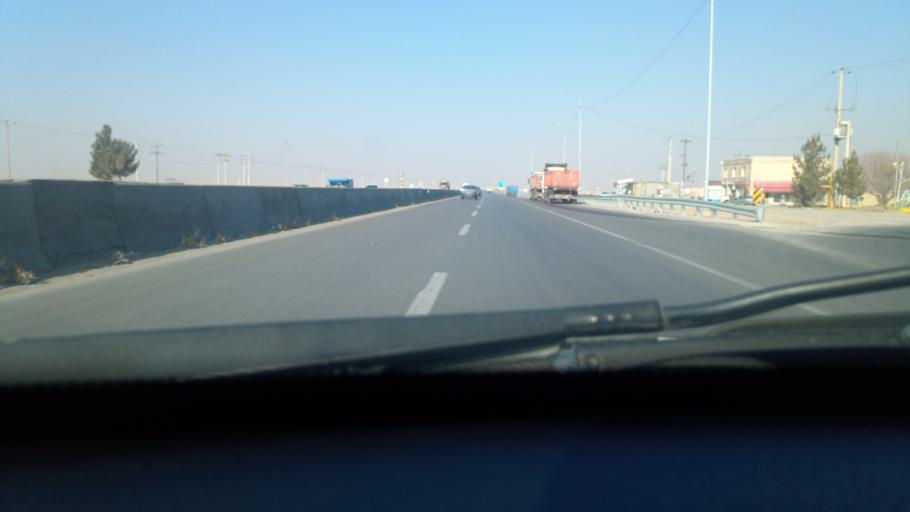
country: IR
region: Razavi Khorasan
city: Chenaran
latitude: 36.7786
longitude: 58.9004
